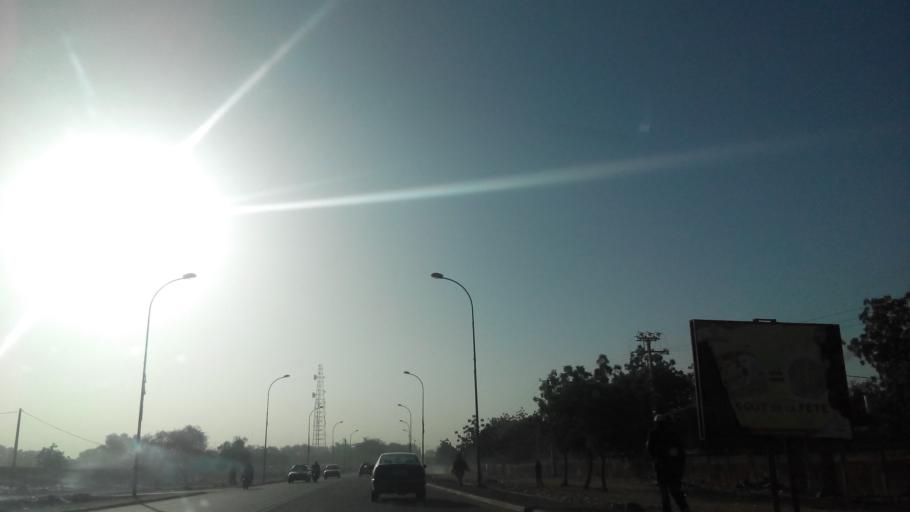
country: NE
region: Niamey
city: Niamey
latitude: 13.5402
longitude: 2.0741
